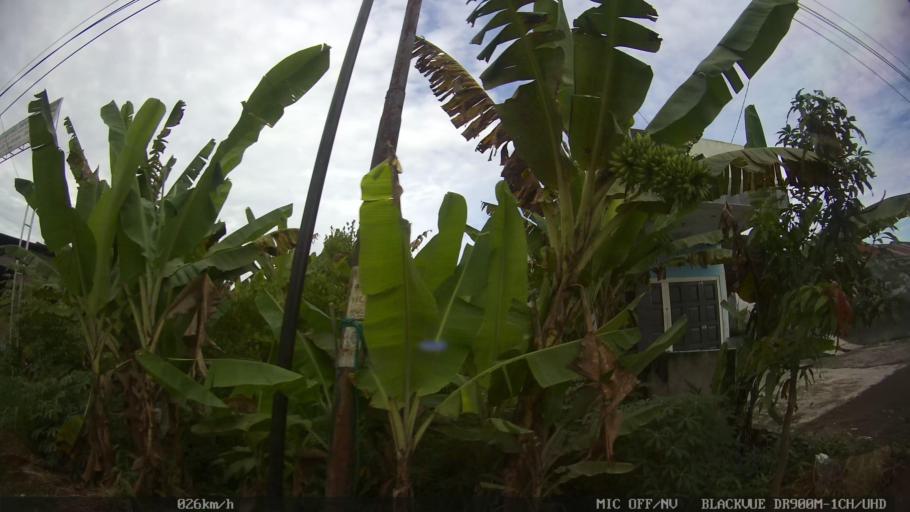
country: ID
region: North Sumatra
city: Sunggal
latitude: 3.5802
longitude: 98.5649
